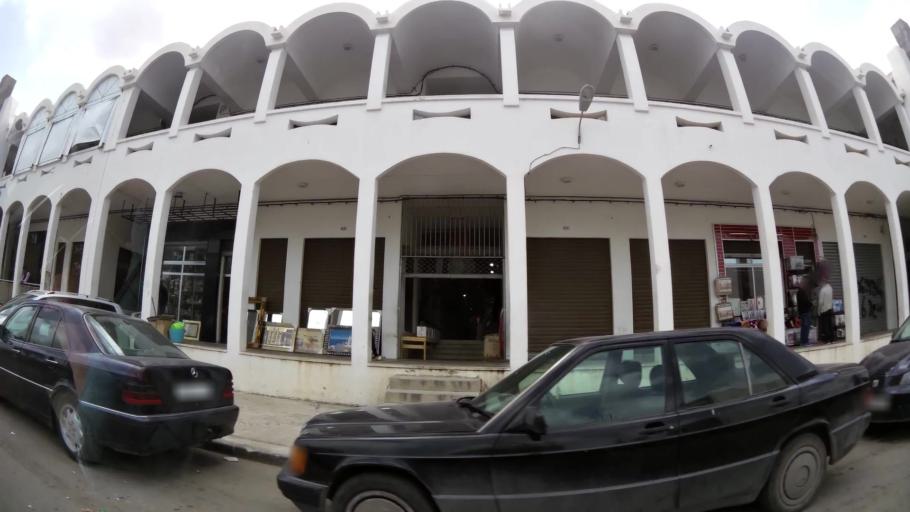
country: MA
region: Oriental
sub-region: Nador
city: Nador
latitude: 35.1777
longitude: -2.9225
